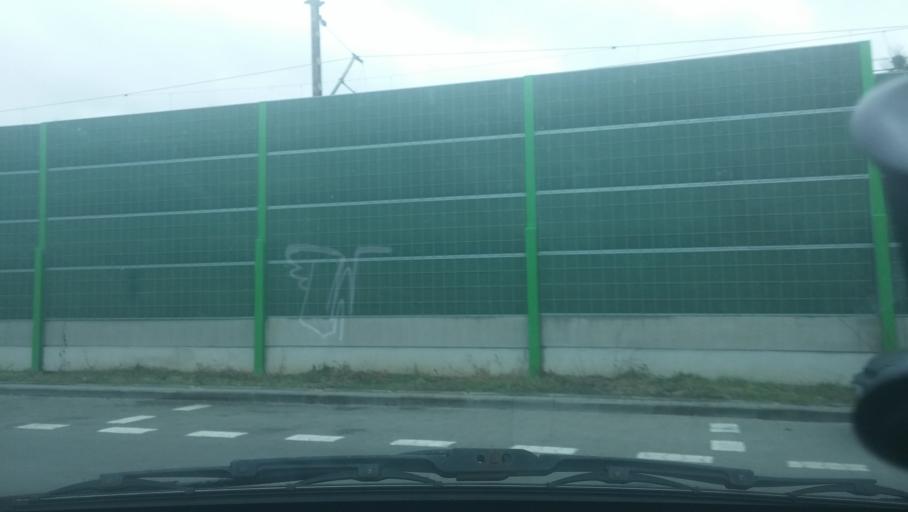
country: PL
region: Masovian Voivodeship
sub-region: Warszawa
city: Ursus
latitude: 52.1979
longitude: 20.8899
